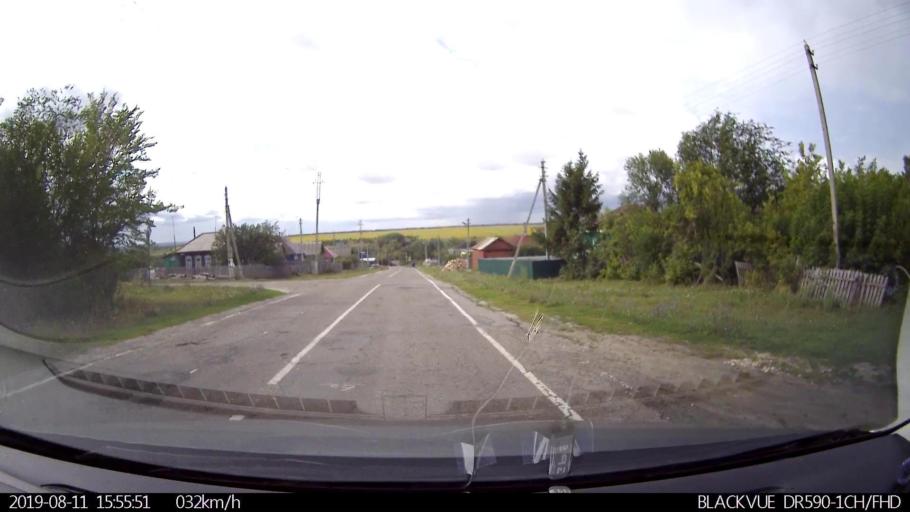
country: RU
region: Ulyanovsk
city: Ignatovka
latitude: 53.9466
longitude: 47.6519
